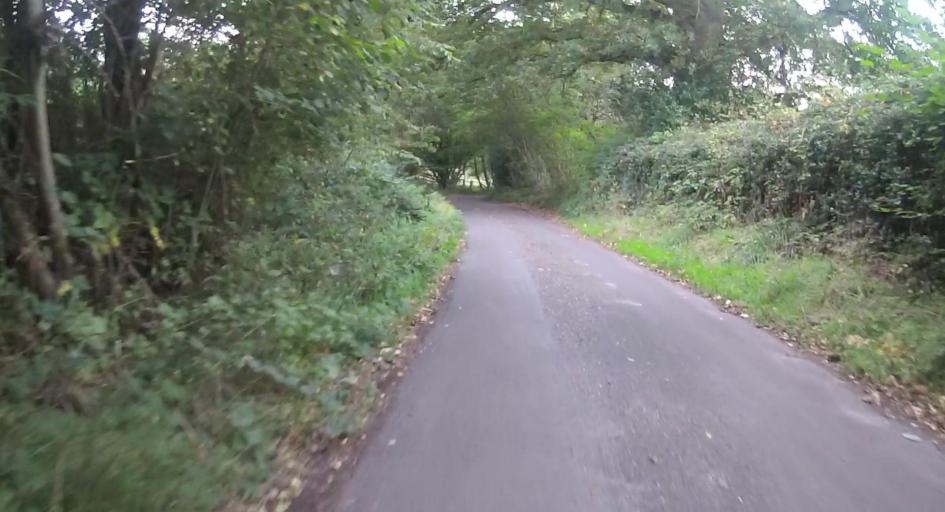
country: GB
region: England
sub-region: Hampshire
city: Hook
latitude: 51.3144
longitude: -0.9286
